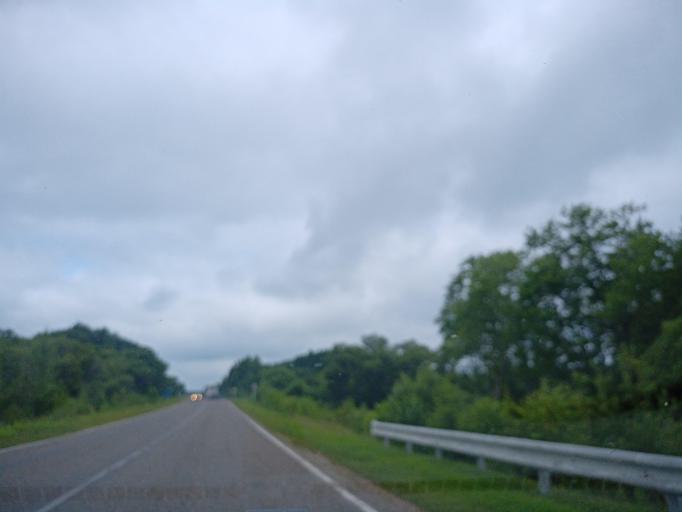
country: RU
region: Primorskiy
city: Novopokrovka
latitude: 45.9709
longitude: 134.2341
